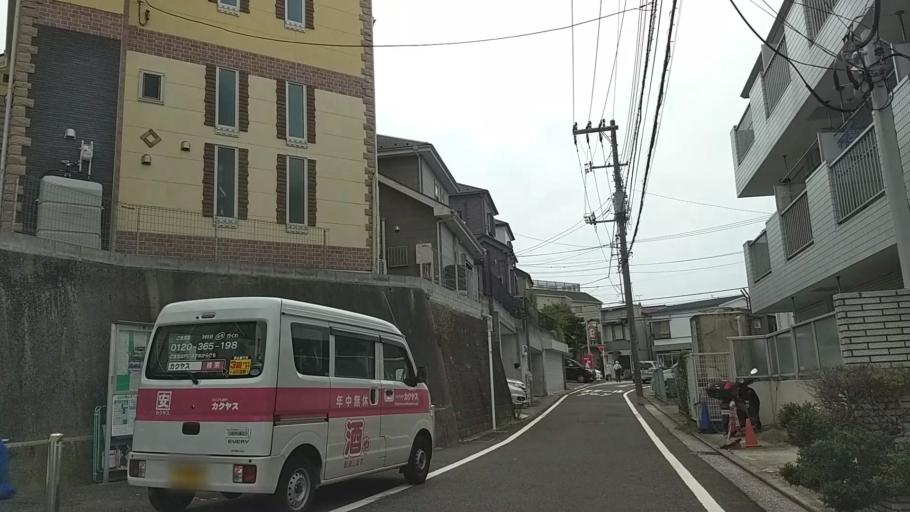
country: JP
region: Kanagawa
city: Yokohama
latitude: 35.4428
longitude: 139.6170
